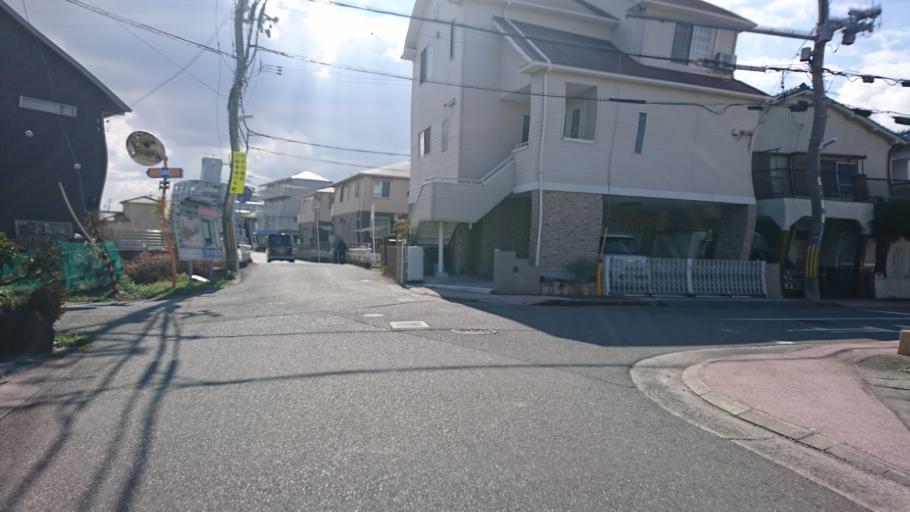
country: JP
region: Hyogo
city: Kakogawacho-honmachi
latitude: 34.7882
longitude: 134.8070
